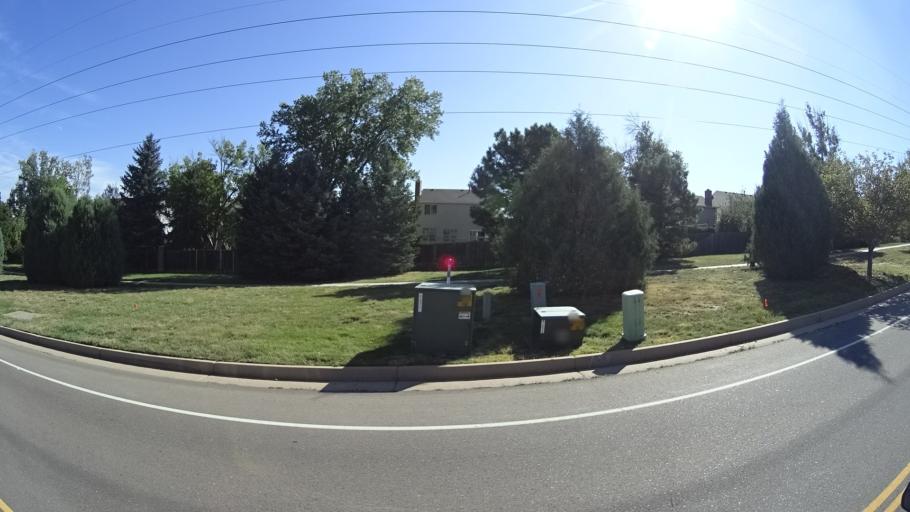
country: US
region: Colorado
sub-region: El Paso County
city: Colorado Springs
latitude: 38.9085
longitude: -104.7896
